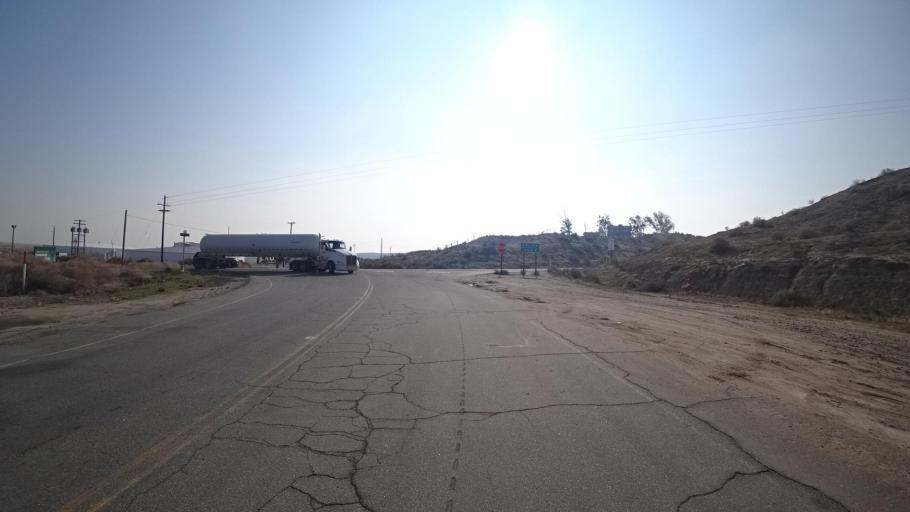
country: US
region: California
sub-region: Kern County
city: Ford City
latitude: 35.2662
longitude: -119.3121
